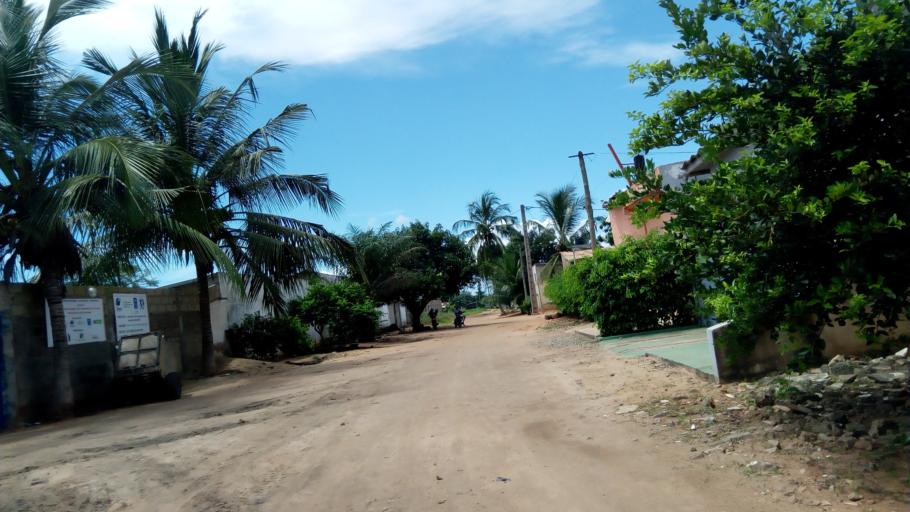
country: TG
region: Maritime
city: Lome
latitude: 6.1701
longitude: 1.1818
